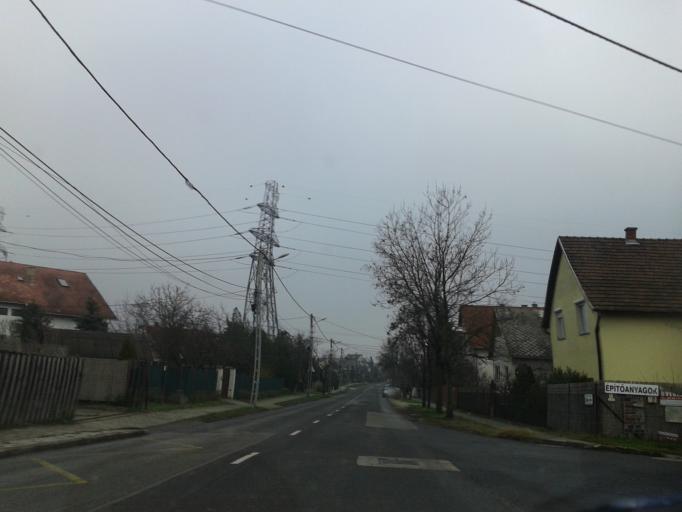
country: HU
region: Budapest
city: Budapest XXII. keruelet
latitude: 47.4309
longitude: 19.0056
